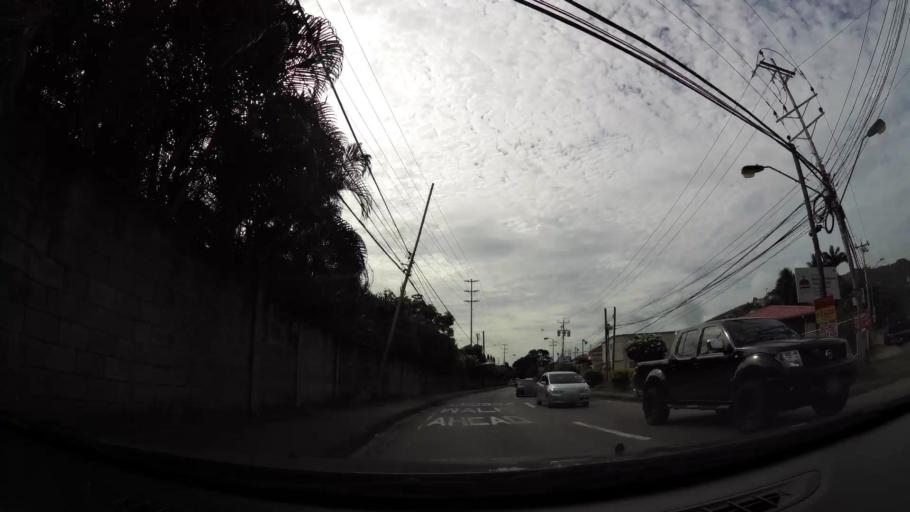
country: TT
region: City of Port of Spain
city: Mucurapo
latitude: 10.6804
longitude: -61.5696
